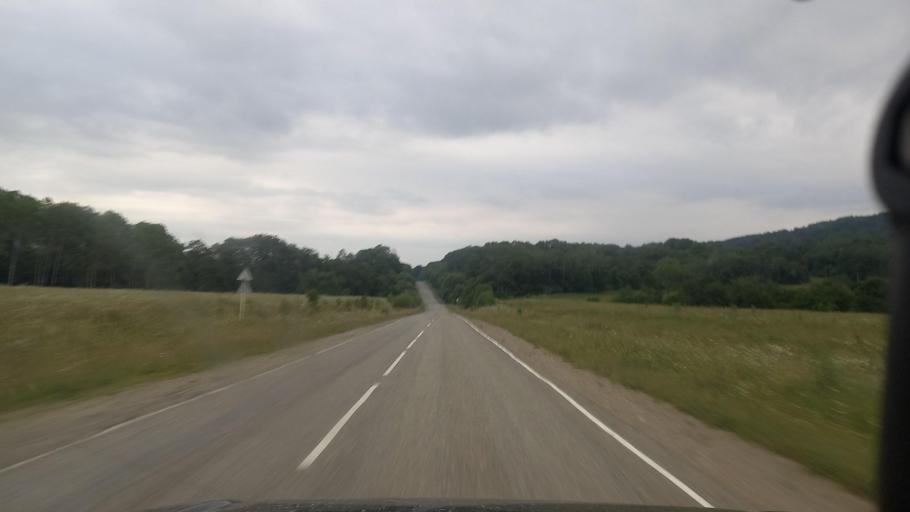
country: RU
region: Karachayevo-Cherkesiya
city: Mednogorskiy
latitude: 43.9430
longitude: 41.1326
